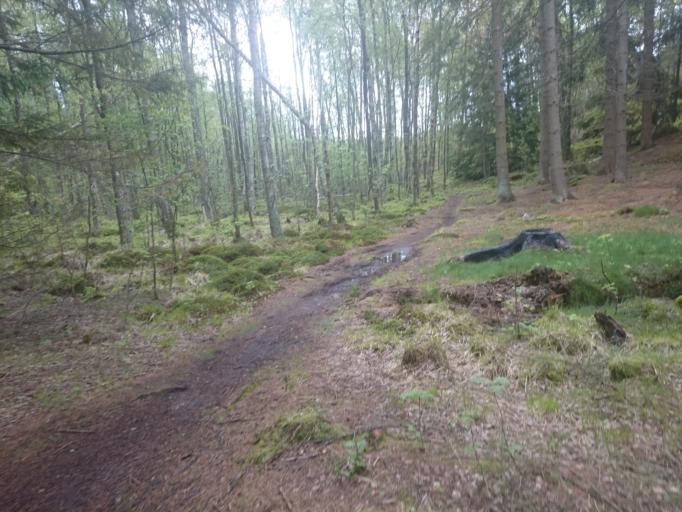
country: SE
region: Vaestra Goetaland
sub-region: Goteborg
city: Goeteborg
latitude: 57.6744
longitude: 11.9577
